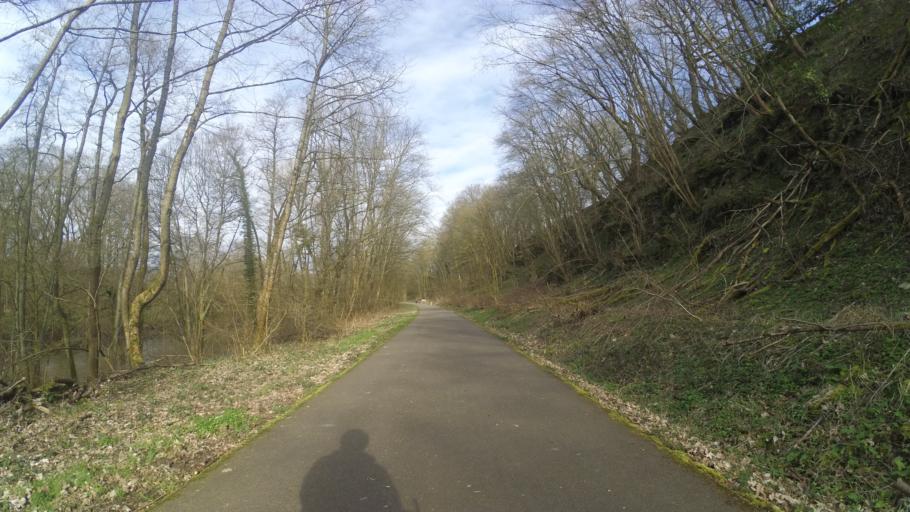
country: DE
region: Saarland
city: Gersheim
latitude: 49.1392
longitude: 7.2034
